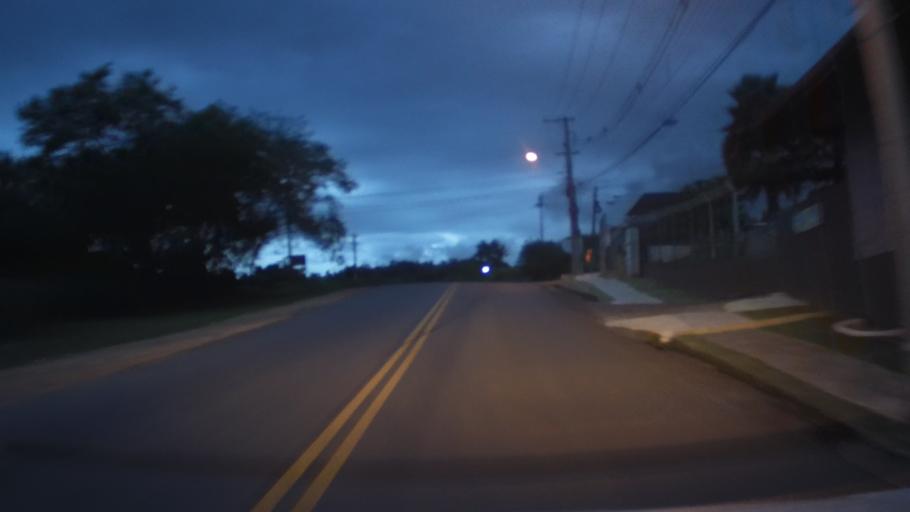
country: BR
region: Sao Paulo
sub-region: Vinhedo
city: Vinhedo
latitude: -23.0615
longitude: -47.0109
